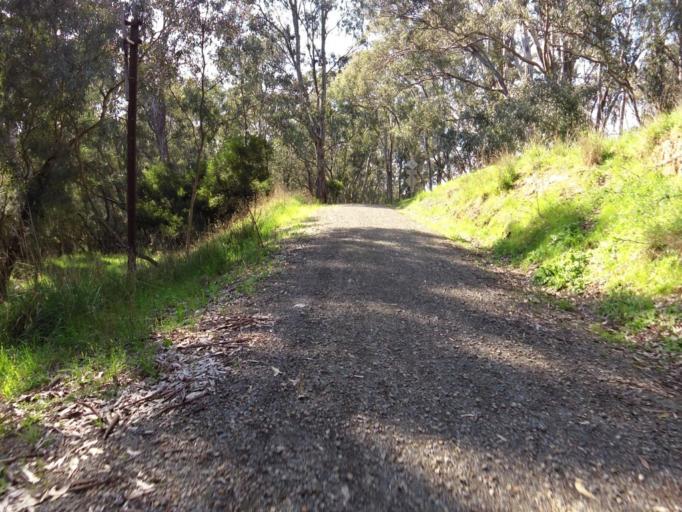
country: AU
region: Victoria
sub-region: Murrindindi
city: Alexandra
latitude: -37.1615
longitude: 145.5608
